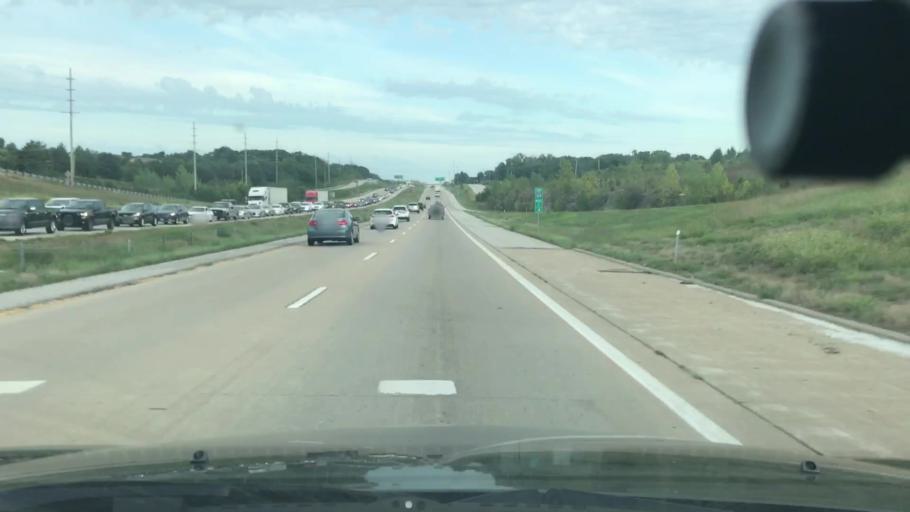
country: US
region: Missouri
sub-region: Saint Charles County
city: Lake Saint Louis
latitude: 38.7954
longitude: -90.8186
